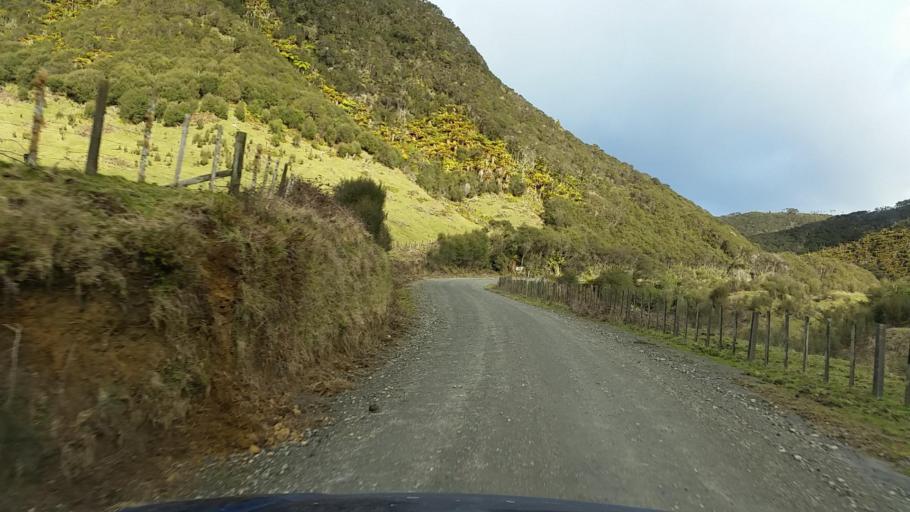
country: NZ
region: Taranaki
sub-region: South Taranaki District
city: Eltham
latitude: -39.2667
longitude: 174.7441
